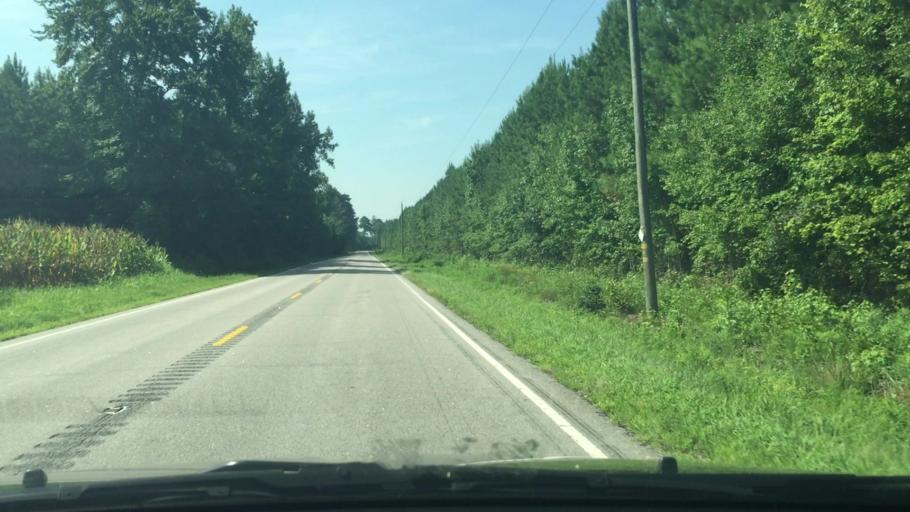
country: US
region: Virginia
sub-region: Southampton County
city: Courtland
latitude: 36.8174
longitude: -77.1256
